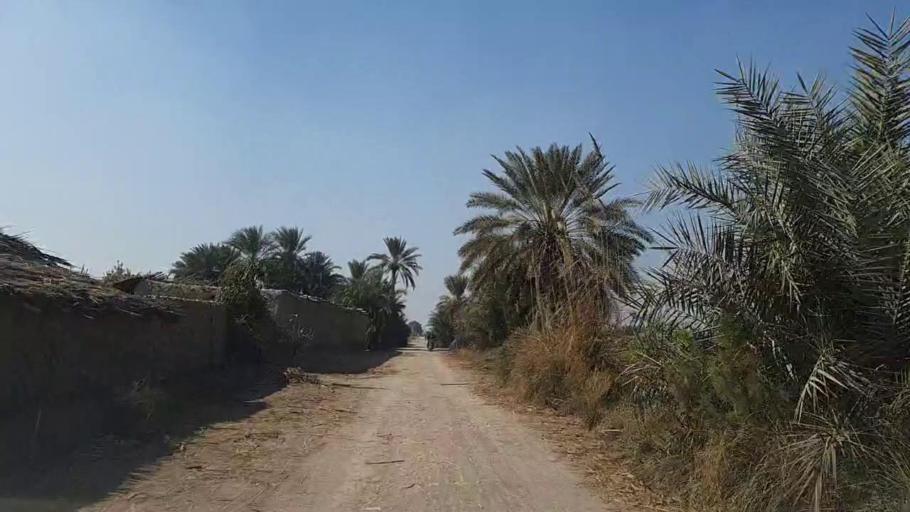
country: PK
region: Sindh
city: Daur
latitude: 26.5029
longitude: 68.3348
